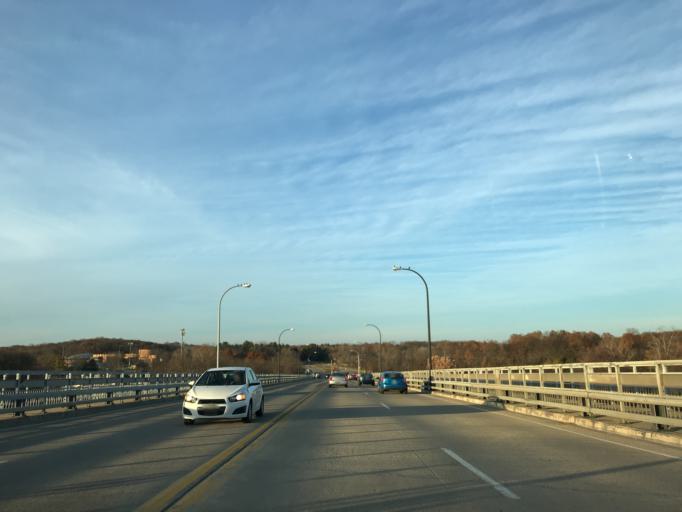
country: US
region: Michigan
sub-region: Washtenaw County
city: Ann Arbor
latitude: 42.2741
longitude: -83.6985
